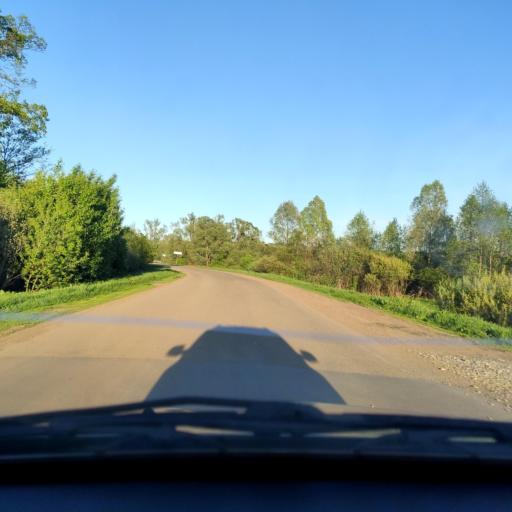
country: RU
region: Bashkortostan
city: Yazykovo
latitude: 55.0255
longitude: 56.2122
